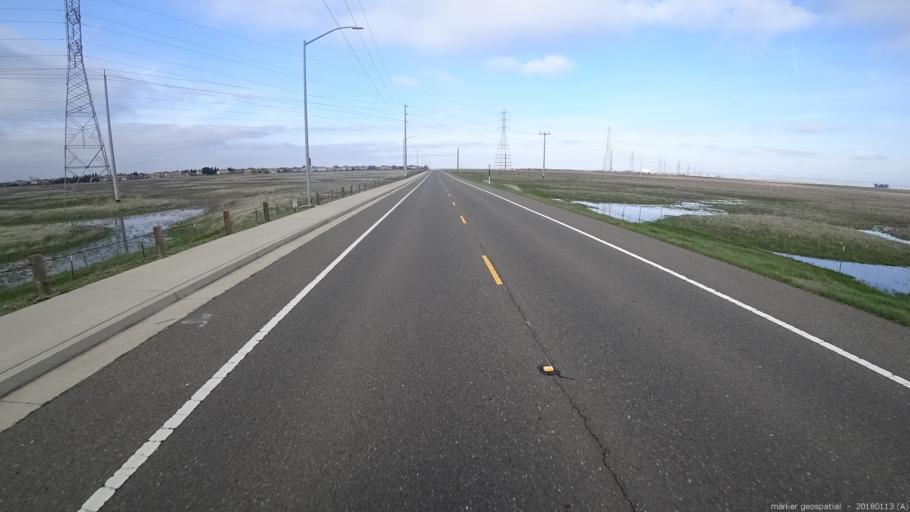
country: US
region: California
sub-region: Sacramento County
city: Gold River
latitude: 38.5387
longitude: -121.2241
